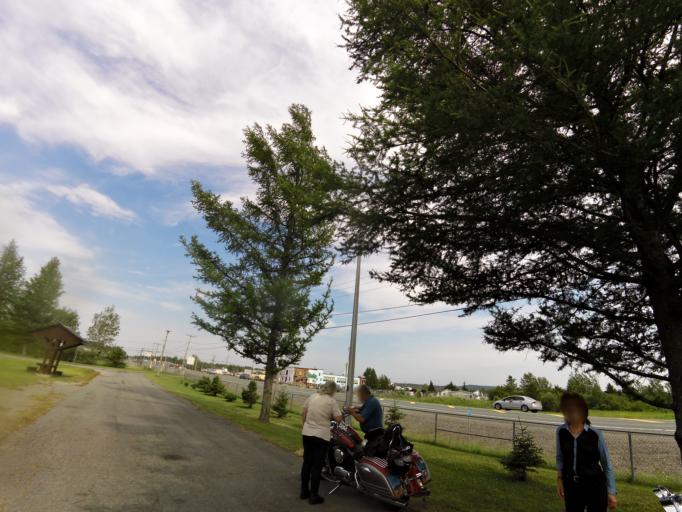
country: CA
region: Quebec
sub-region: Abitibi-Temiscamingue
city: Malartic
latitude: 48.2269
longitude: -78.3894
